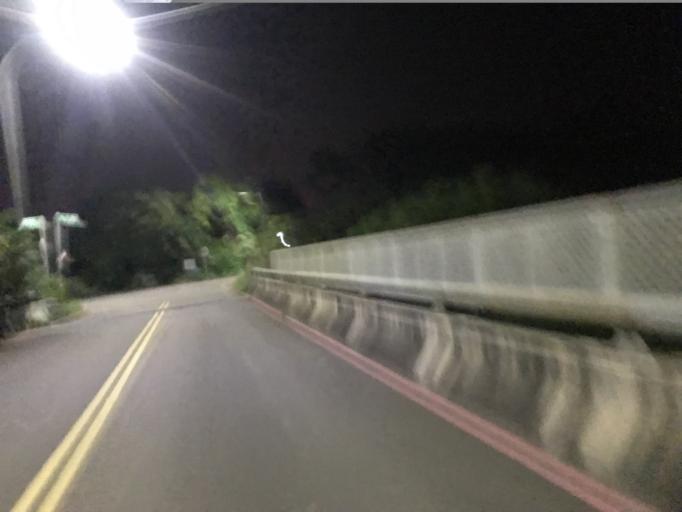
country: TW
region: Taiwan
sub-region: Hsinchu
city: Hsinchu
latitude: 24.7529
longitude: 120.9439
